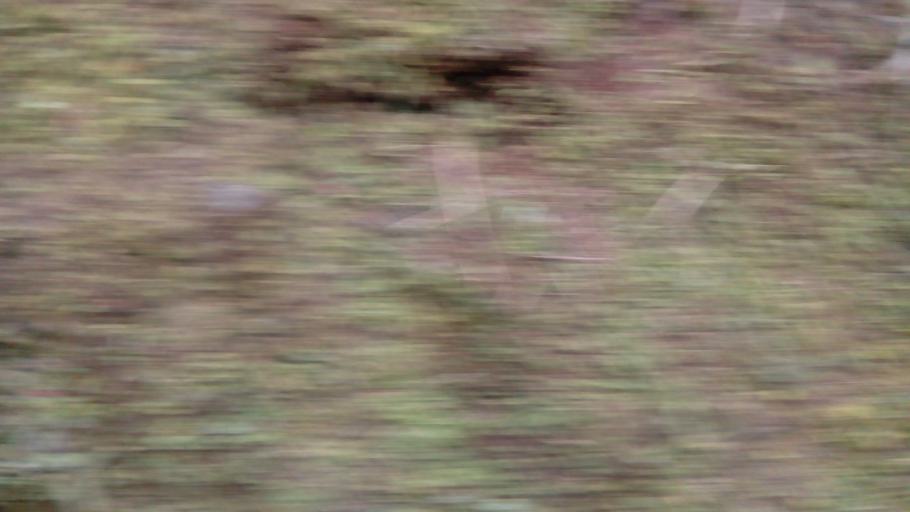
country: TW
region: Taiwan
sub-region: Yilan
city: Yilan
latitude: 24.5605
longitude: 121.4773
